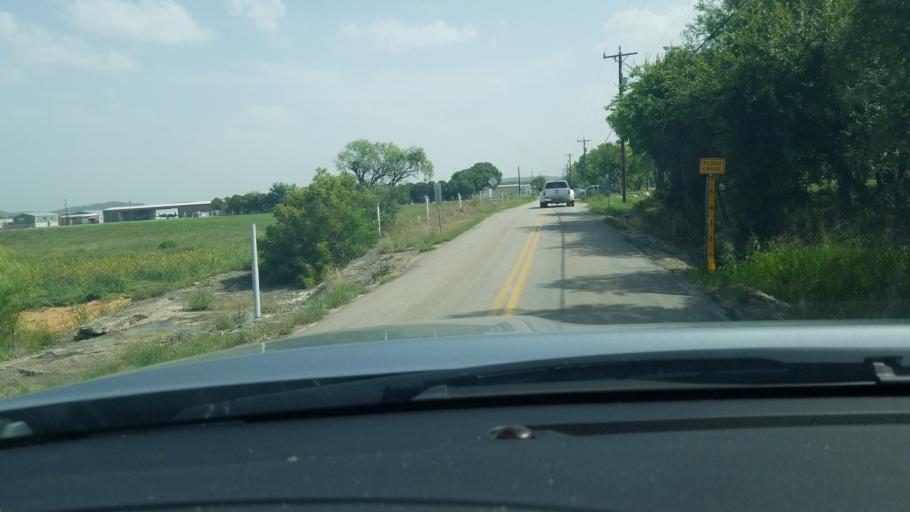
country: US
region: Texas
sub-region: Comal County
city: Bulverde
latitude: 29.7405
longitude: -98.4541
